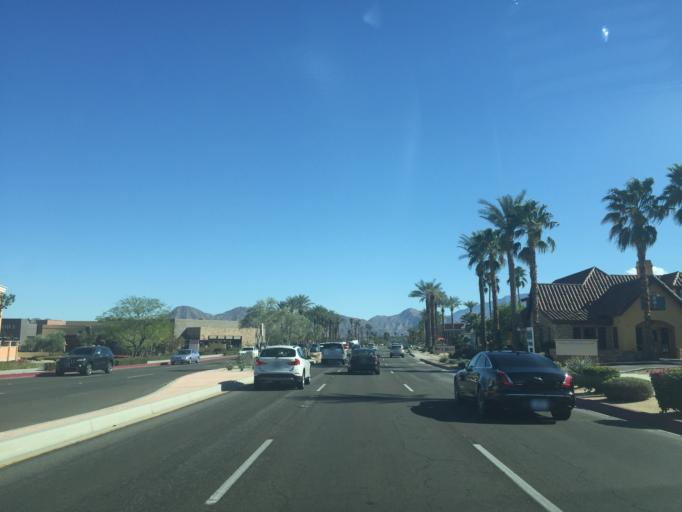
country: US
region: California
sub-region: Riverside County
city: Rancho Mirage
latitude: 33.7397
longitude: -116.4111
